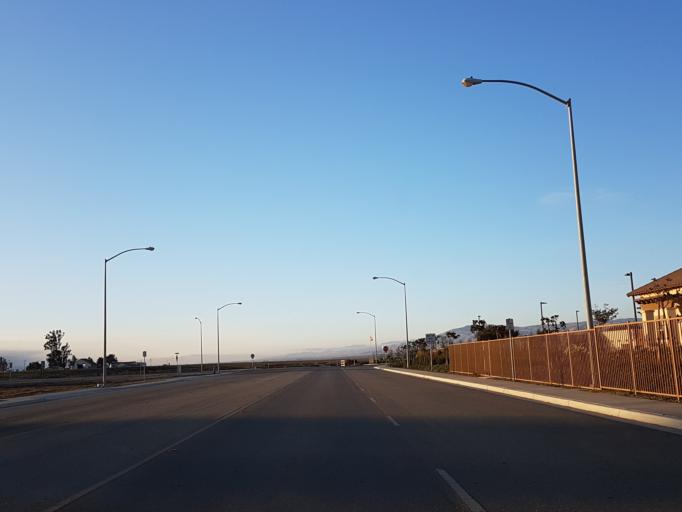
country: US
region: California
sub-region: Monterey County
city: Greenfield
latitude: 36.3413
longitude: -121.2535
